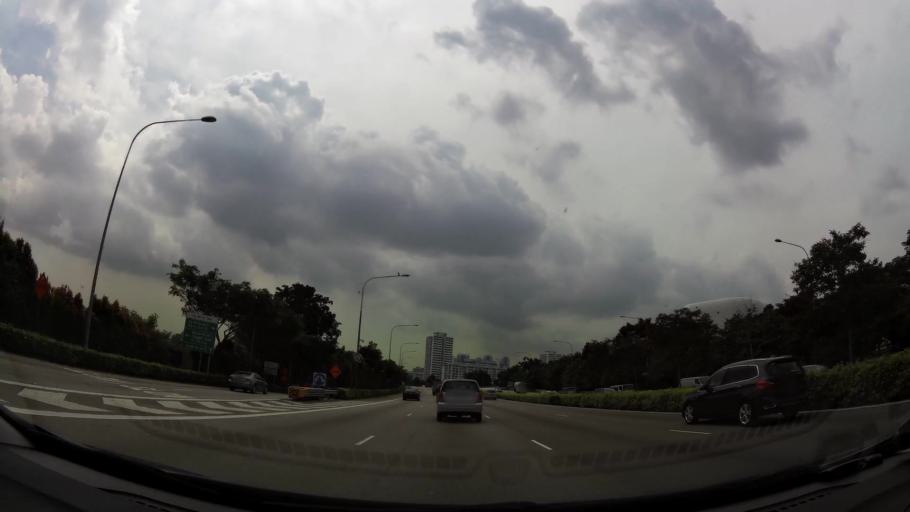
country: SG
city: Singapore
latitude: 1.3784
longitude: 103.8586
